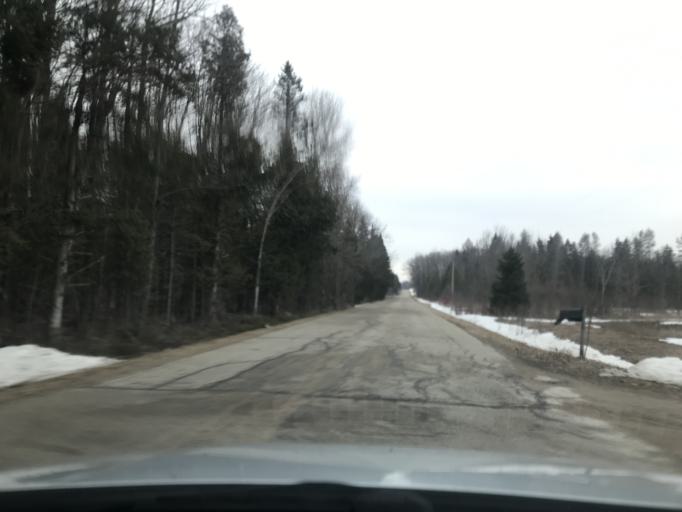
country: US
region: Wisconsin
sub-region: Marinette County
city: Peshtigo
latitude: 45.1182
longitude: -88.0081
